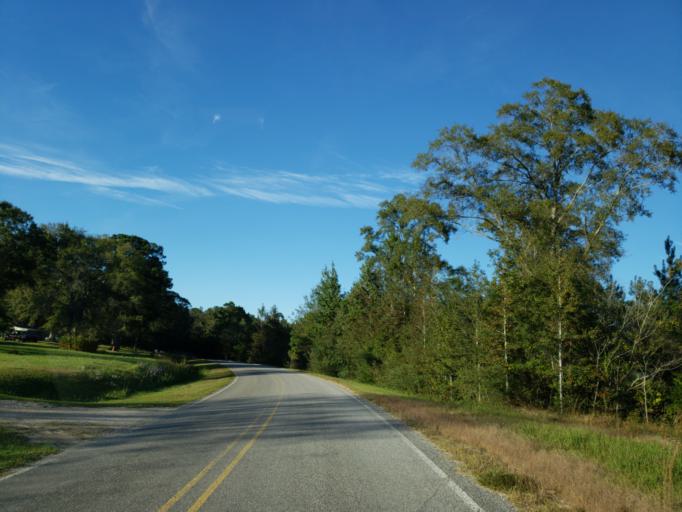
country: US
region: Mississippi
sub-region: Perry County
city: Richton
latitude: 31.3427
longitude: -88.8082
